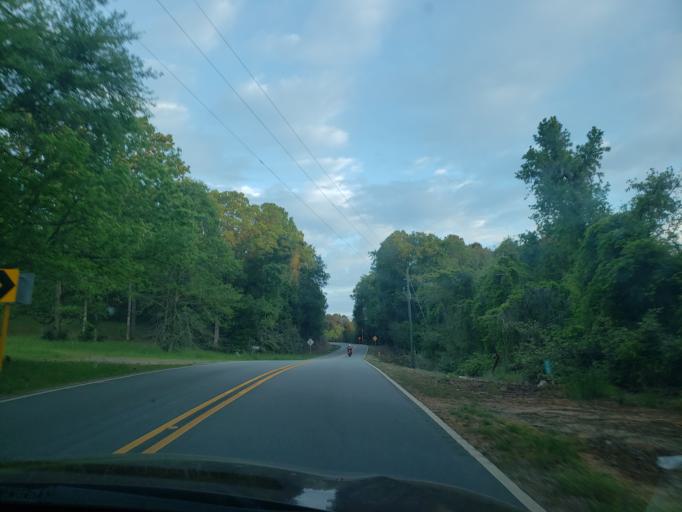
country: US
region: Alabama
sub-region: Tallapoosa County
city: Dadeville
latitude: 32.7086
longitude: -85.7716
